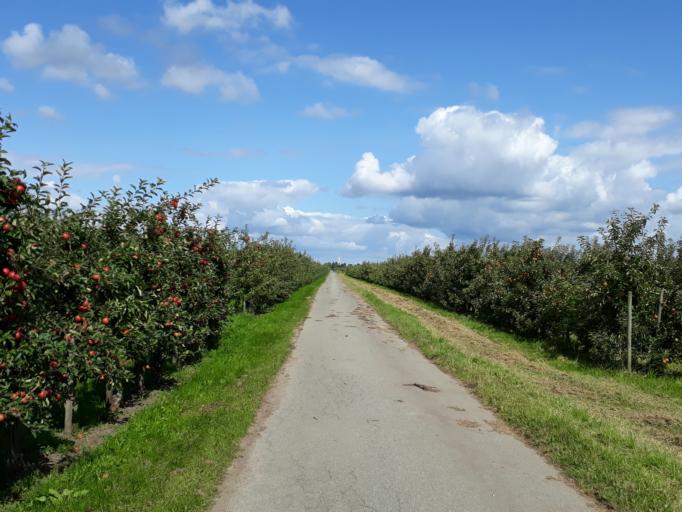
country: DE
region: Lower Saxony
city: Jork
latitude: 53.5013
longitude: 9.6833
